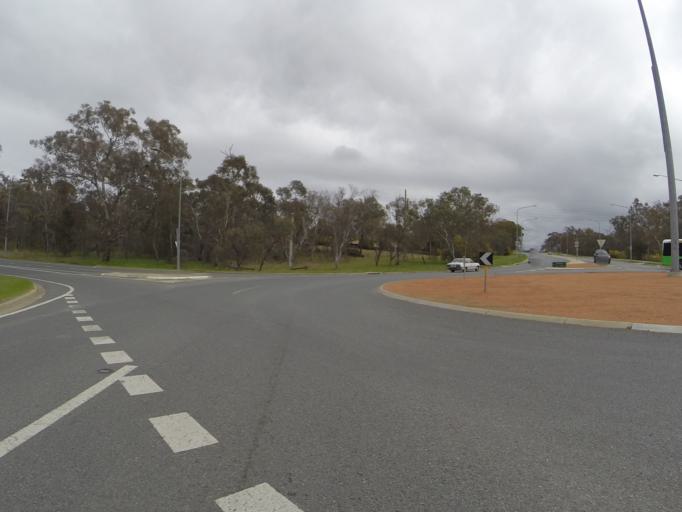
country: AU
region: Australian Capital Territory
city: Canberra
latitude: -35.2874
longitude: 149.1658
